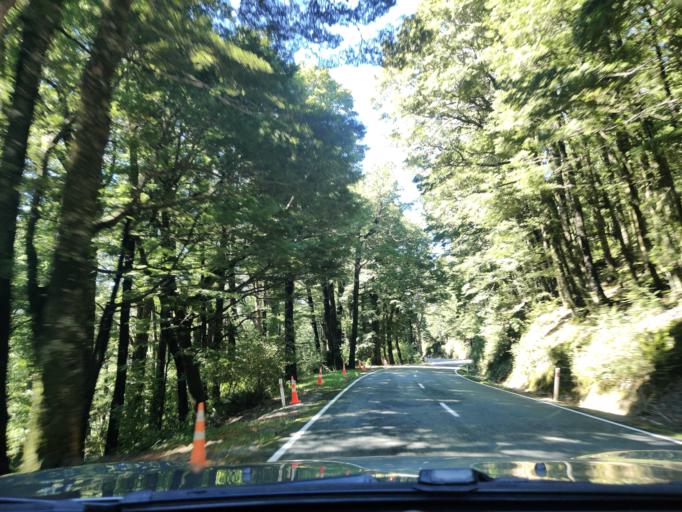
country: NZ
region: Canterbury
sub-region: Hurunui District
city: Amberley
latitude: -42.3771
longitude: 172.3568
